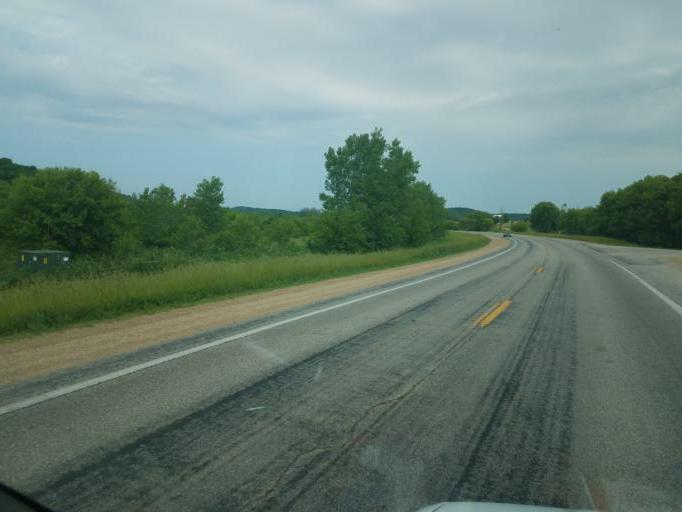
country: US
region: Wisconsin
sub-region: Vernon County
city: Hillsboro
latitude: 43.6571
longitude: -90.3669
